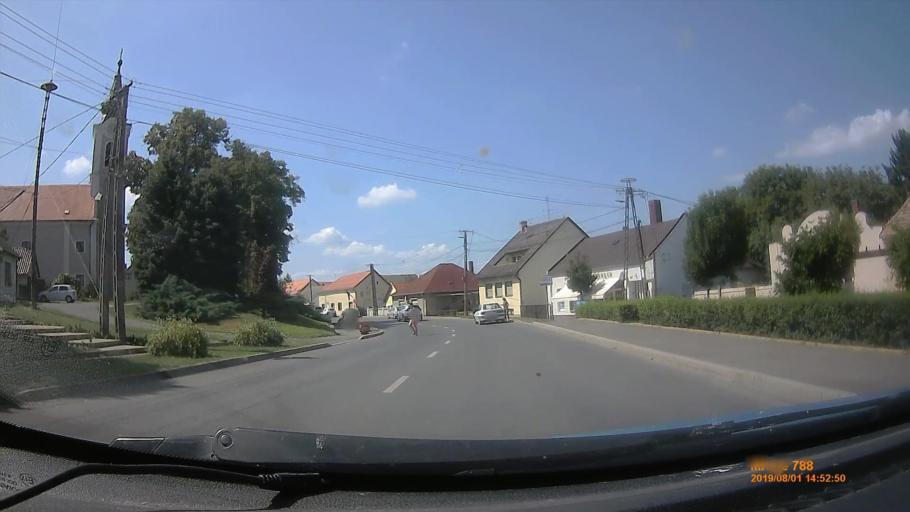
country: HU
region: Baranya
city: Vajszlo
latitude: 45.8595
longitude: 17.9838
